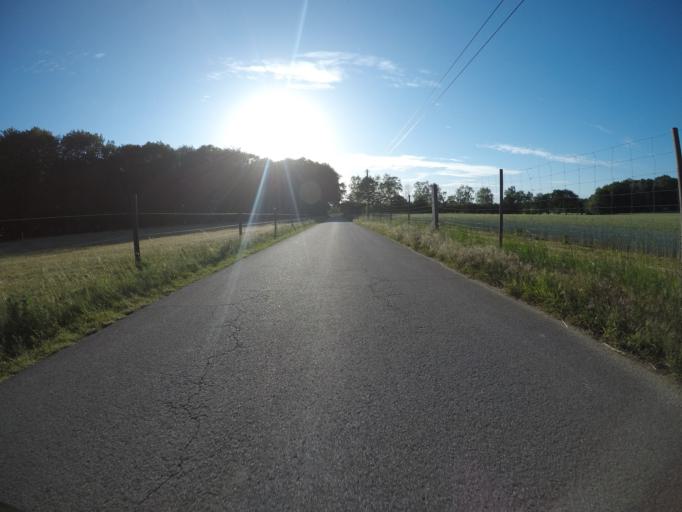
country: DE
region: North Rhine-Westphalia
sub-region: Regierungsbezirk Dusseldorf
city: Schermbeck
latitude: 51.7189
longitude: 6.8813
